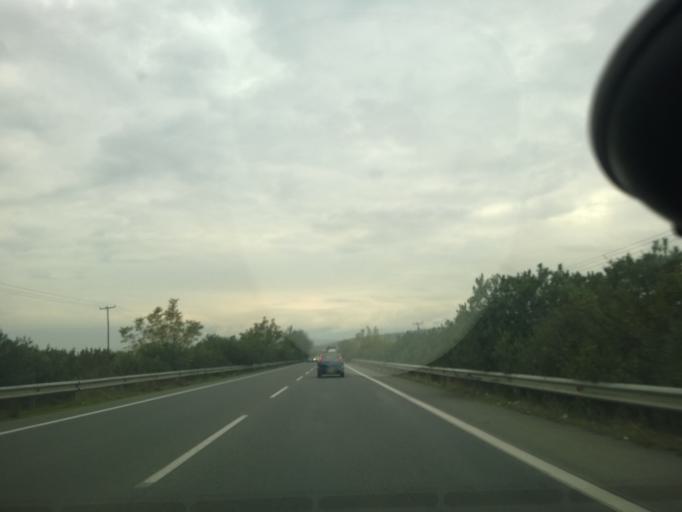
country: GR
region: Central Macedonia
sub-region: Nomos Pellis
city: Mavrovouni
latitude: 40.7924
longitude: 22.1725
